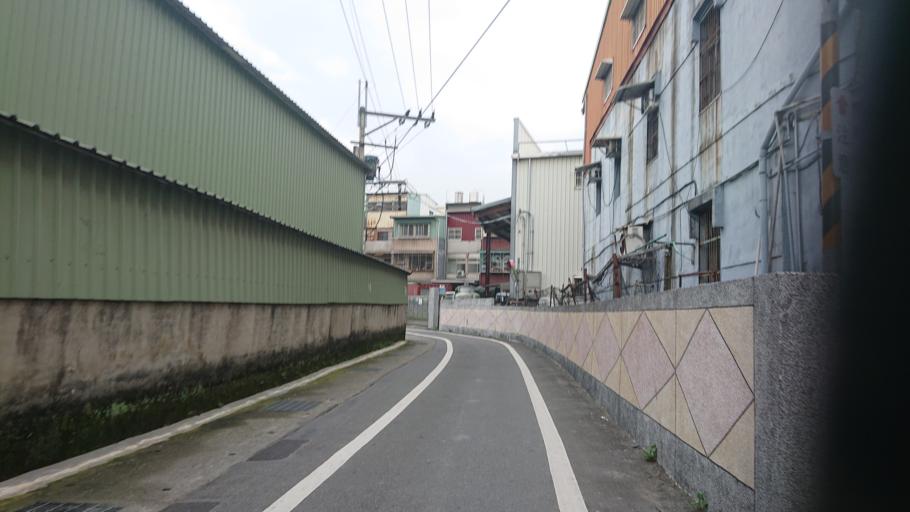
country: TW
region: Taiwan
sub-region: Taoyuan
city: Taoyuan
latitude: 24.9526
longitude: 121.3733
